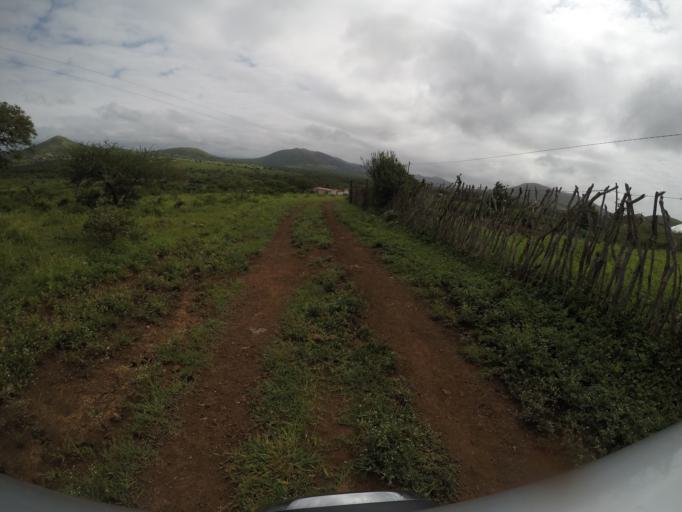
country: ZA
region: KwaZulu-Natal
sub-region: uThungulu District Municipality
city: Empangeni
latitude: -28.6218
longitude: 31.8712
